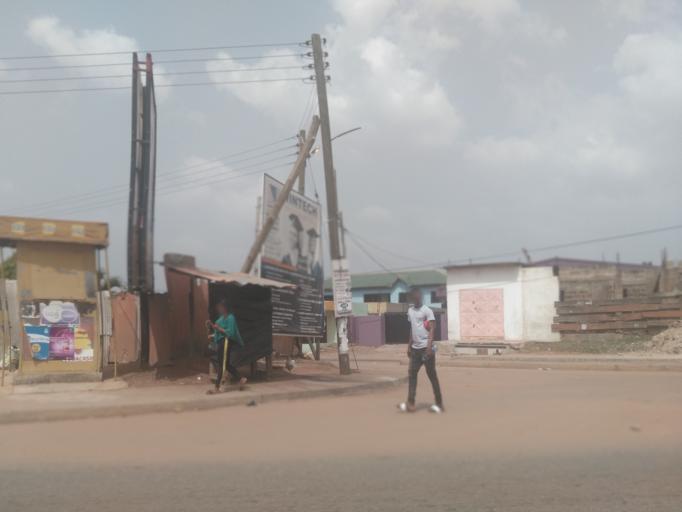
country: GH
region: Greater Accra
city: Dome
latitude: 5.6018
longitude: -0.2604
